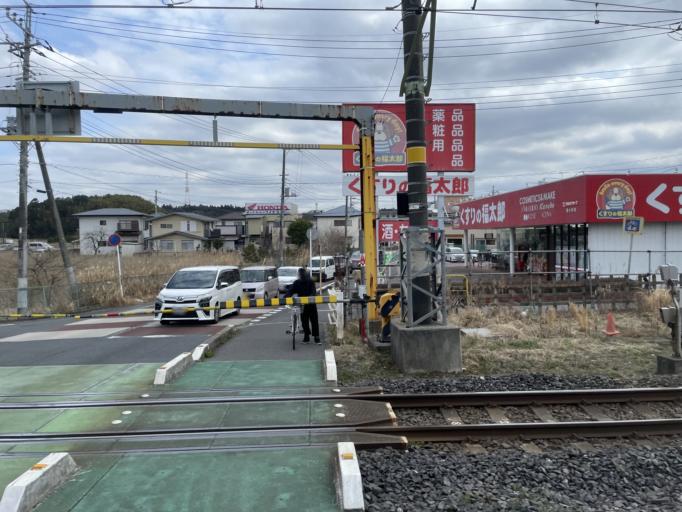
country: JP
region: Chiba
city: Shisui
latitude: 35.7327
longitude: 140.2761
